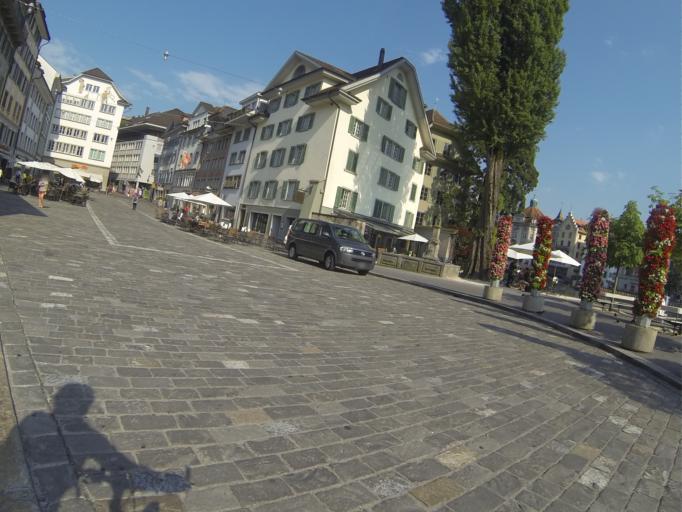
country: CH
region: Lucerne
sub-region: Lucerne-Stadt District
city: Luzern
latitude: 47.0520
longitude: 8.3027
